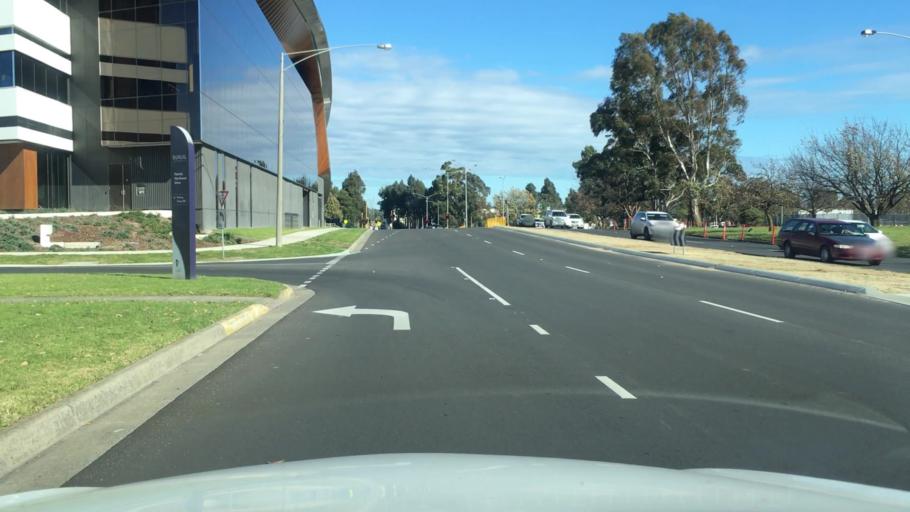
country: AU
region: Victoria
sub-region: Casey
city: Narre Warren
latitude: -38.0188
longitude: 145.2998
